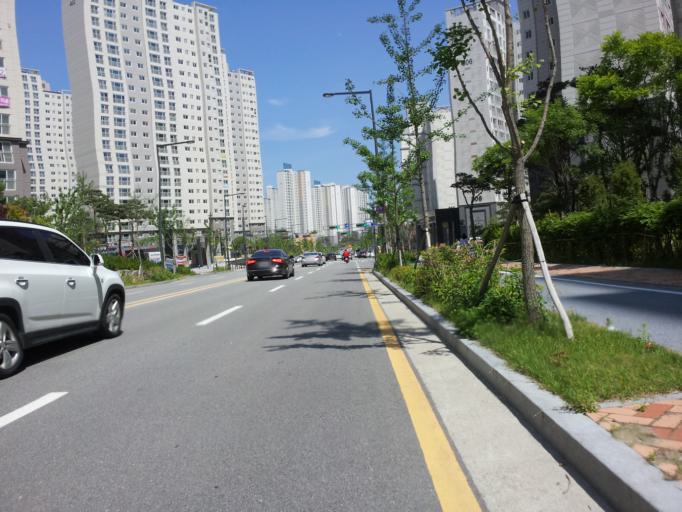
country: KR
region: Chungcheongnam-do
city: Gongju
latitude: 36.5052
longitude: 127.2420
